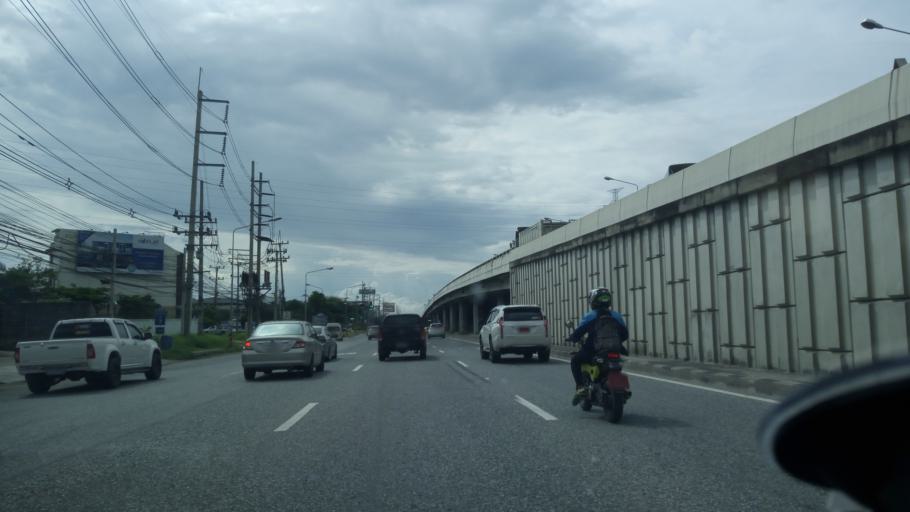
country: TH
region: Chon Buri
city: Chon Buri
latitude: 13.3857
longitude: 101.0161
